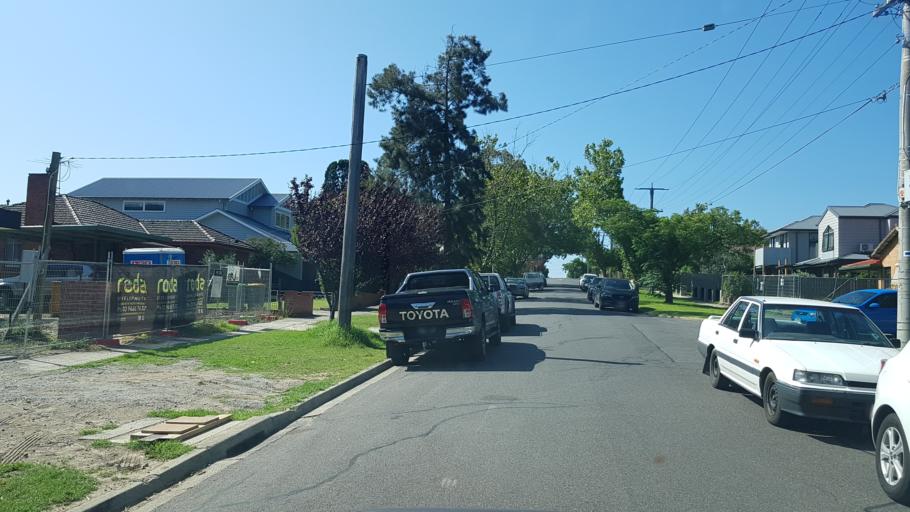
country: AU
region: Victoria
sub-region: Banyule
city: Heidelberg Heights
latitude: -37.7507
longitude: 145.0505
